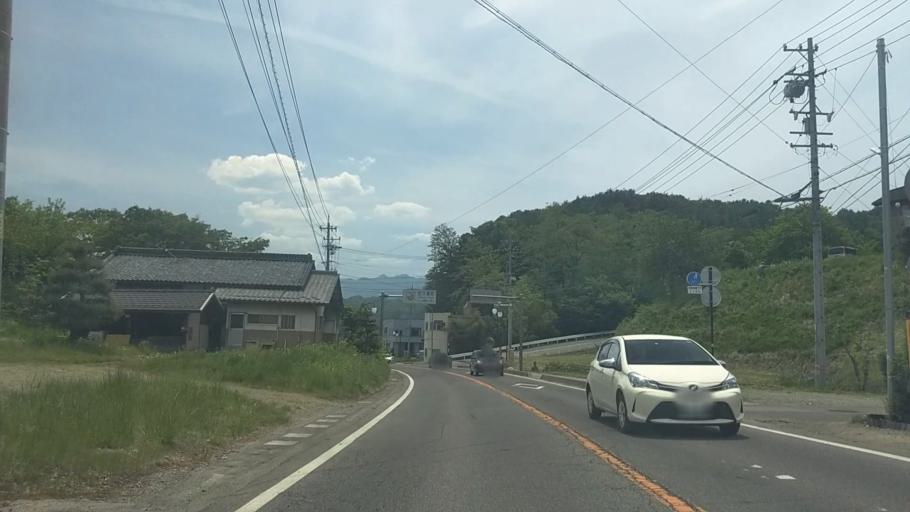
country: JP
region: Nagano
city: Saku
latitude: 36.1800
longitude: 138.4821
